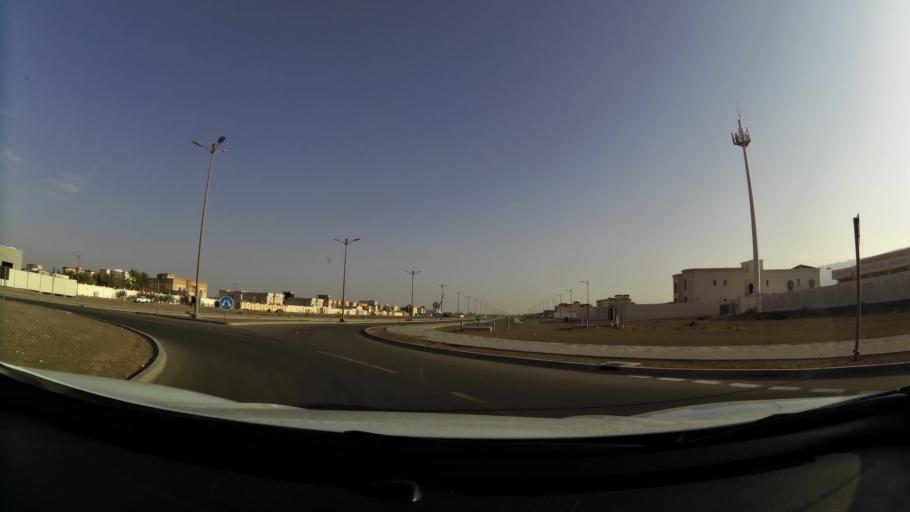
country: AE
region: Abu Dhabi
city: Al Ain
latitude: 24.1089
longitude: 55.8396
